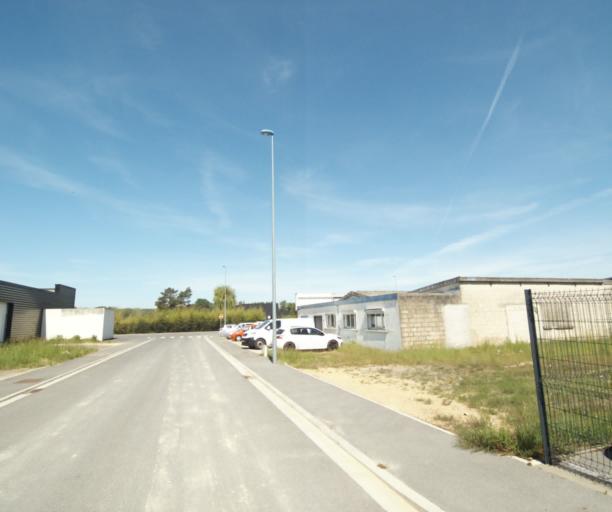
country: FR
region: Champagne-Ardenne
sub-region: Departement des Ardennes
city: Villers-Semeuse
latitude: 49.7356
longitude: 4.7336
